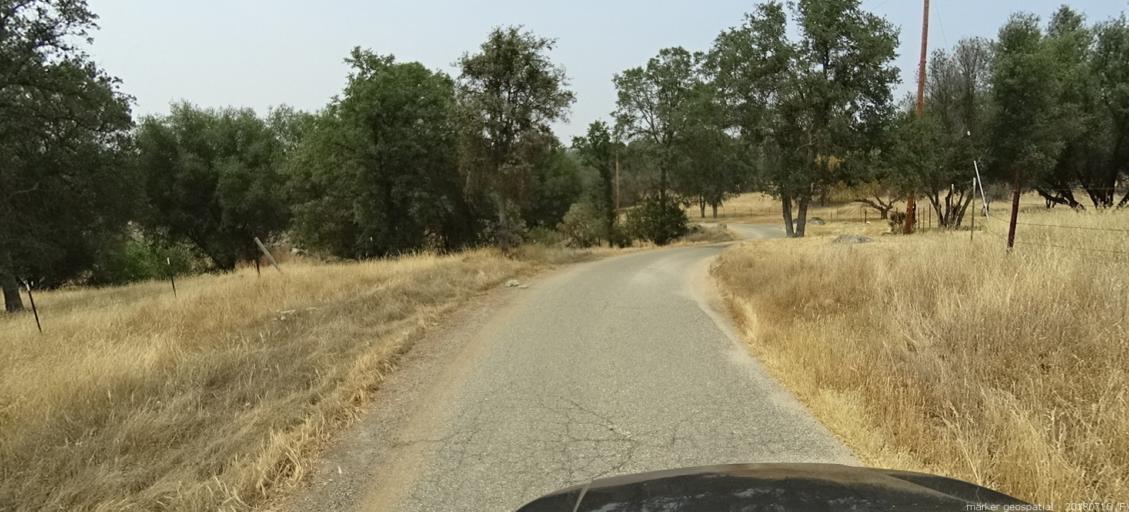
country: US
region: California
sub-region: Madera County
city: Yosemite Lakes
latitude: 37.2334
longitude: -119.8027
